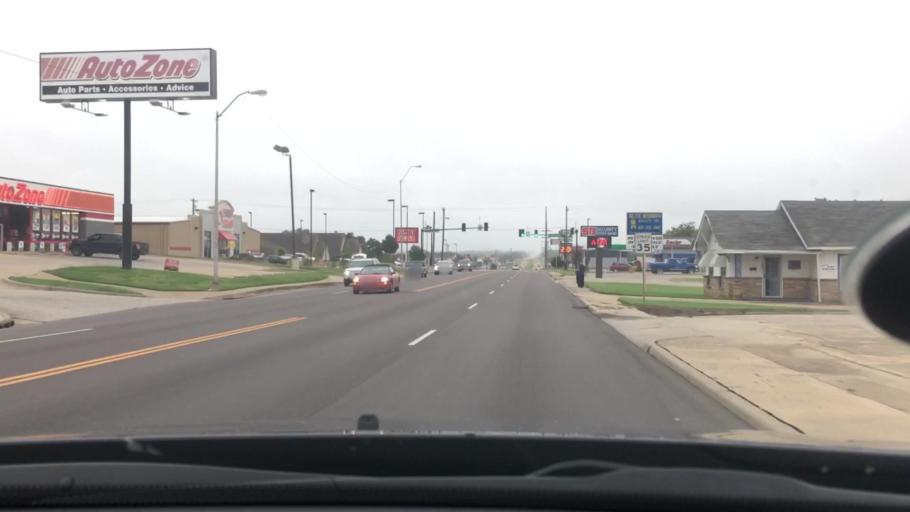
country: US
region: Oklahoma
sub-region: Seminole County
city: Seminole
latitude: 35.2306
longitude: -96.6710
